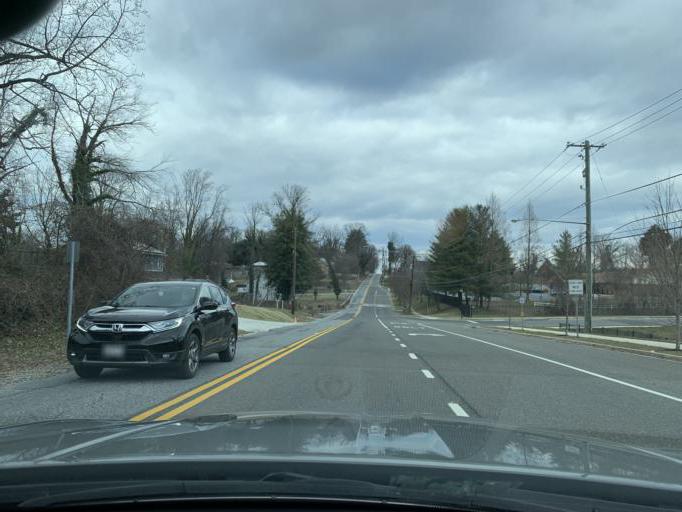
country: US
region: Maryland
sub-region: Prince George's County
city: Capitol Heights
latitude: 38.8816
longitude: -76.9027
